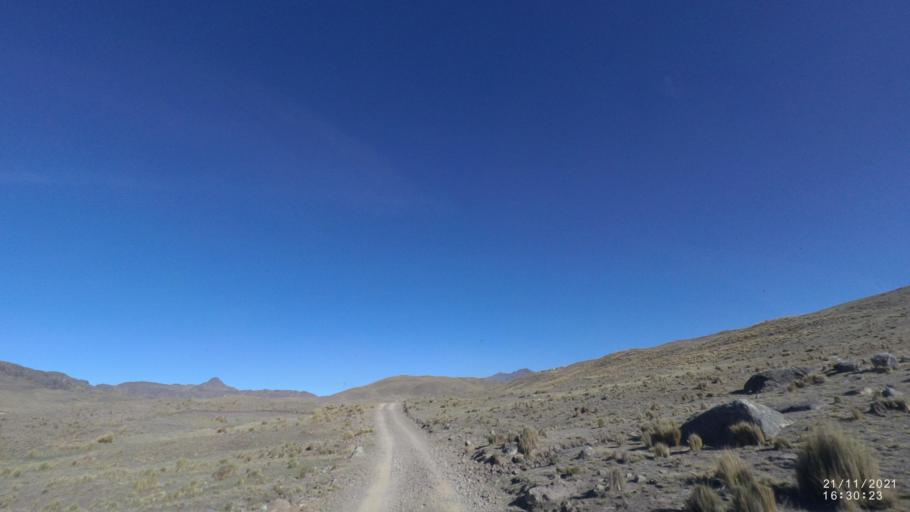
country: BO
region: Cochabamba
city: Cochabamba
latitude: -17.0265
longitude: -66.2808
